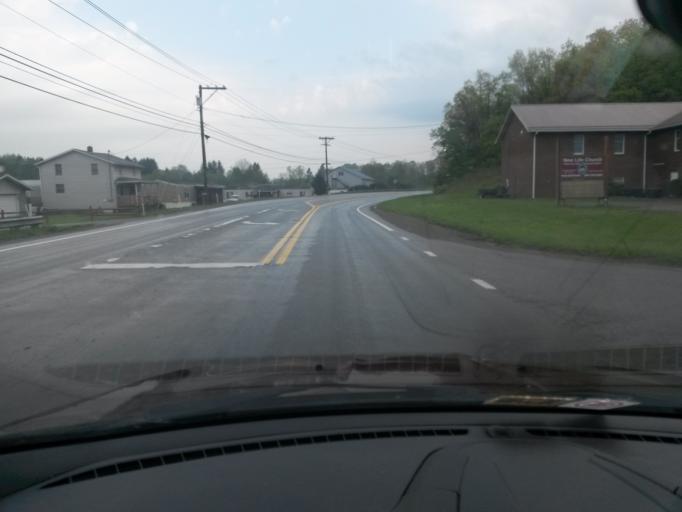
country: US
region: West Virginia
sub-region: Randolph County
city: Elkins
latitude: 38.8257
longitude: -79.8746
